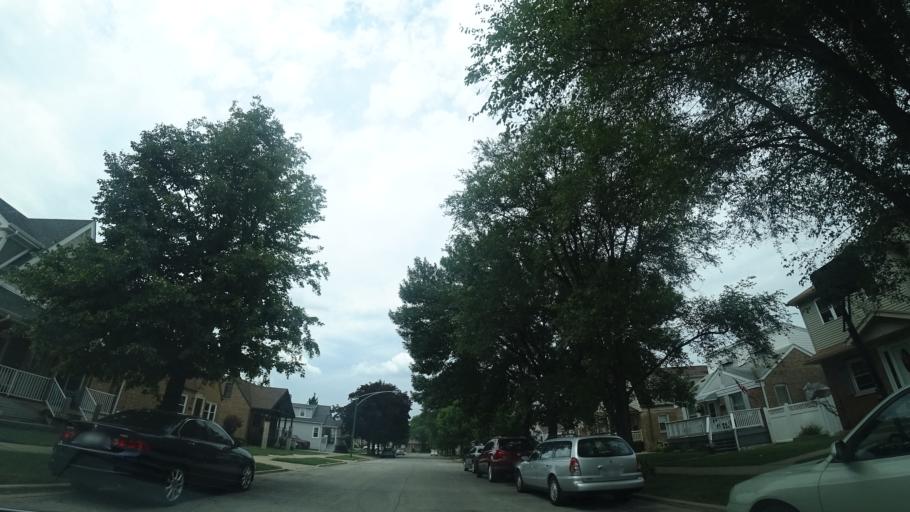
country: US
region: Illinois
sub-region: Cook County
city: Merrionette Park
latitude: 41.6922
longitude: -87.7162
